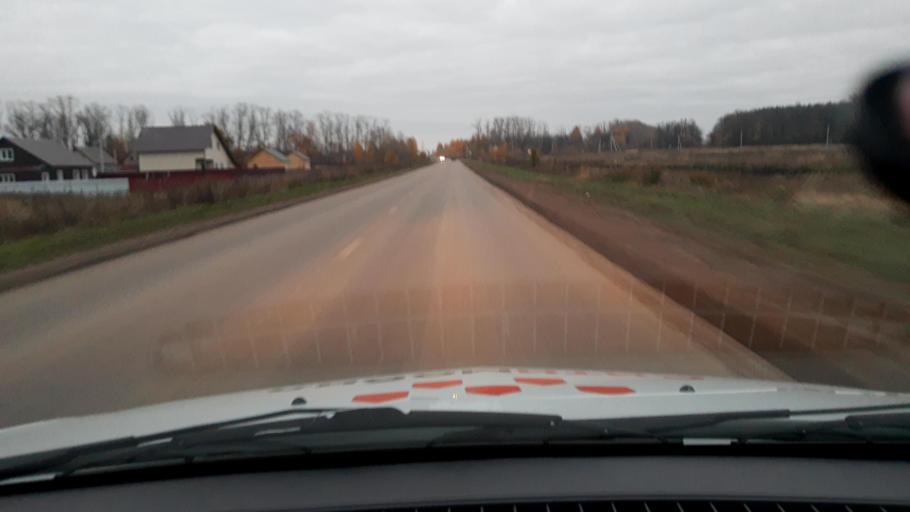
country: RU
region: Bashkortostan
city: Kabakovo
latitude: 54.6971
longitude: 56.1524
